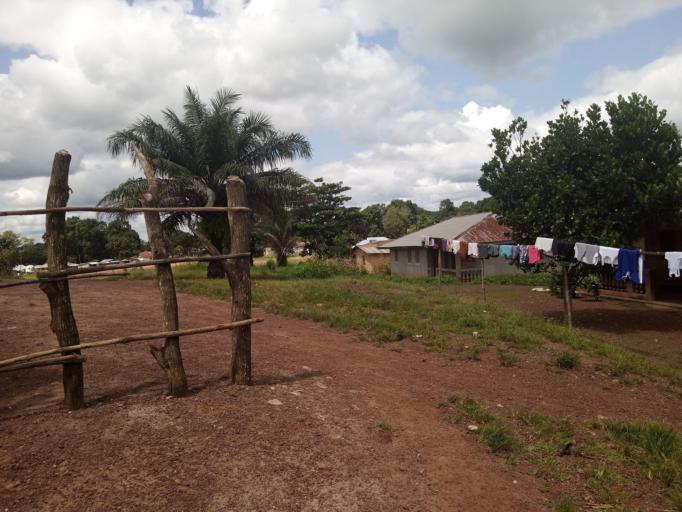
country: SL
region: Northern Province
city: Kamakwie
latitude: 9.4930
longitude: -12.2444
